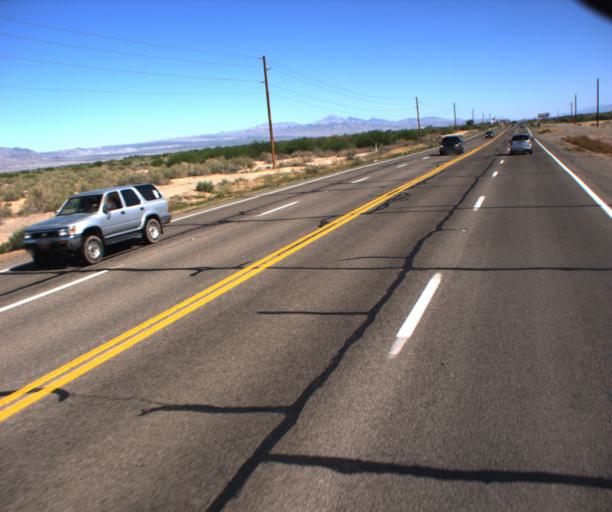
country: US
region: Arizona
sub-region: Mohave County
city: Mohave Valley
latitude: 34.9392
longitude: -114.5979
